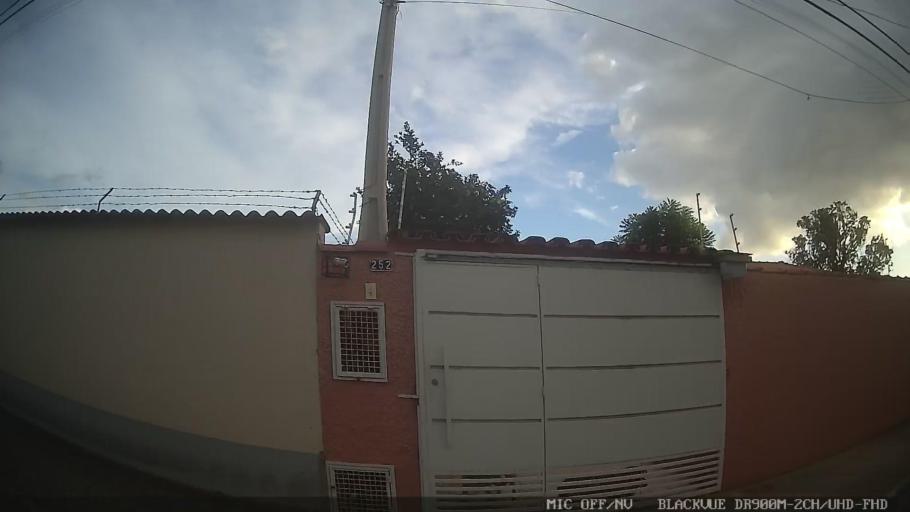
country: BR
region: Sao Paulo
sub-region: Atibaia
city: Atibaia
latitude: -23.1084
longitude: -46.5319
